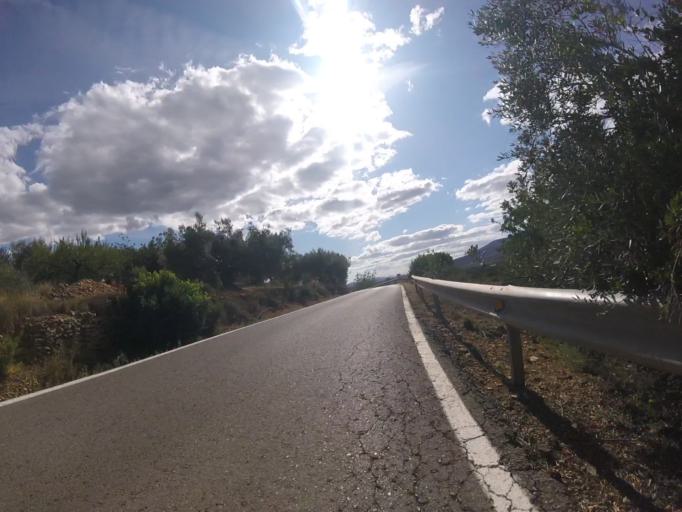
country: ES
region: Valencia
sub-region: Provincia de Castello
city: Cuevas de Vinroma
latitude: 40.3701
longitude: 0.1181
